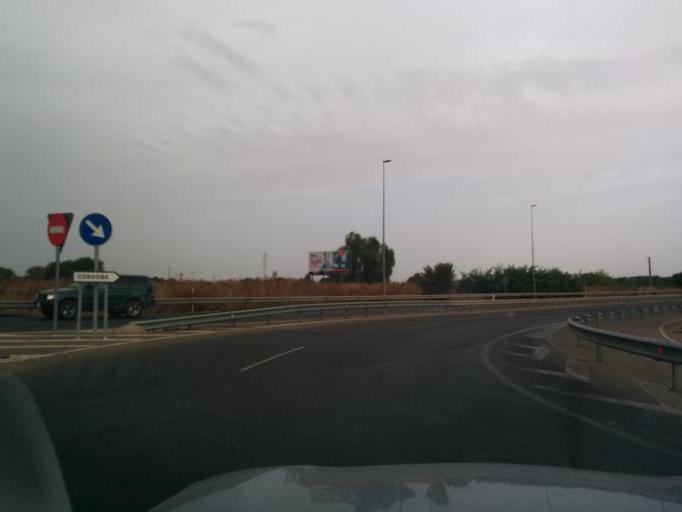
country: ES
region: Andalusia
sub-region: Provincia de Sevilla
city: Sevilla
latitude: 37.4338
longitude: -5.9664
